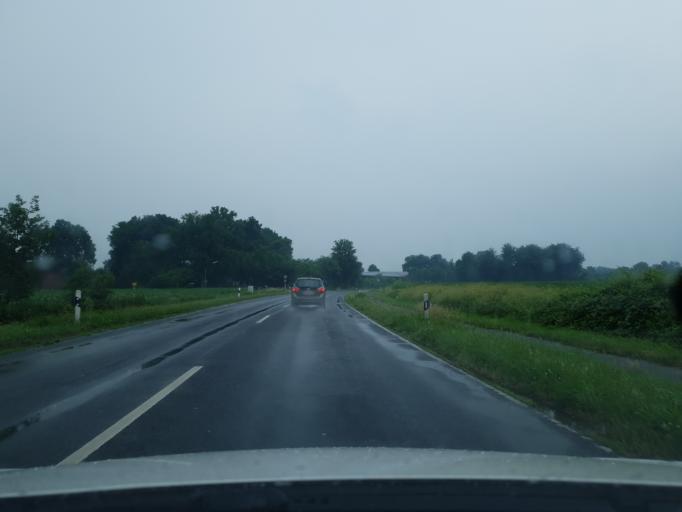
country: DE
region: Lower Saxony
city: Lingen
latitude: 52.5555
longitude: 7.2926
